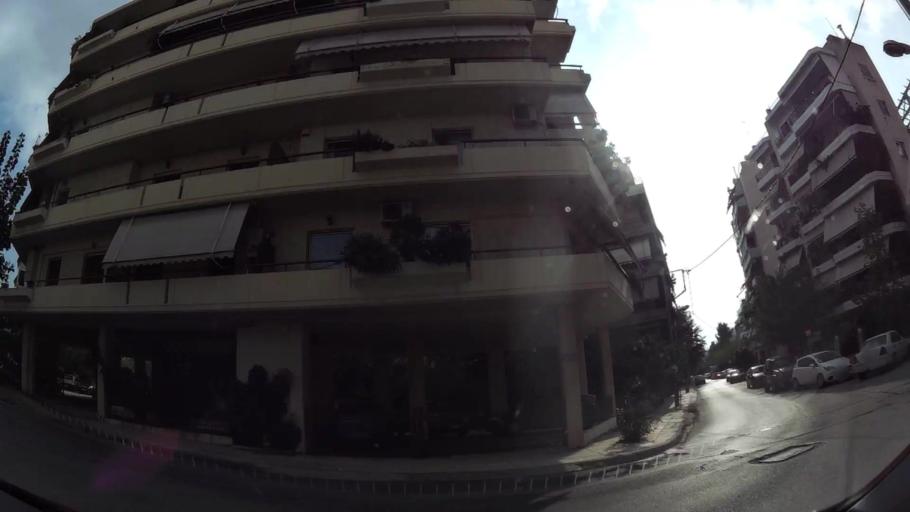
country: GR
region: Attica
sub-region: Nomarchia Athinas
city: Nea Smyrni
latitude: 37.9412
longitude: 23.7231
